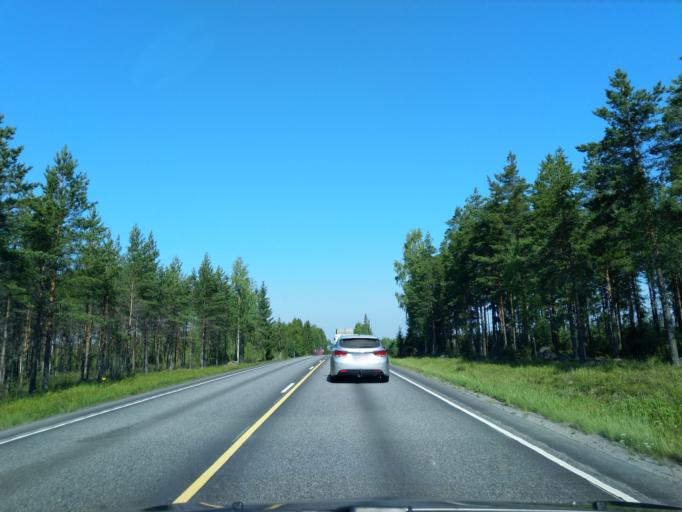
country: FI
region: Satakunta
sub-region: Pori
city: Huittinen
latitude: 61.1270
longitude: 22.8005
